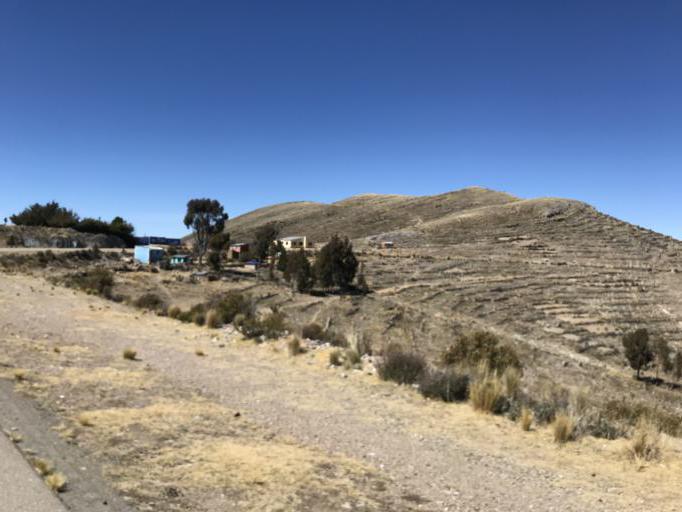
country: BO
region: La Paz
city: San Pedro
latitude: -16.2001
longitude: -68.9047
